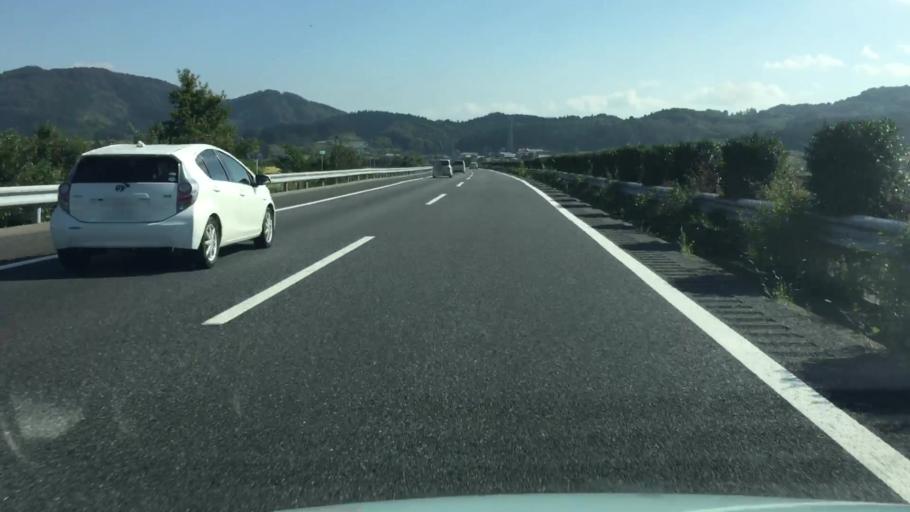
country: JP
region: Ibaraki
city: Iwase
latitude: 36.3429
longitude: 140.1441
